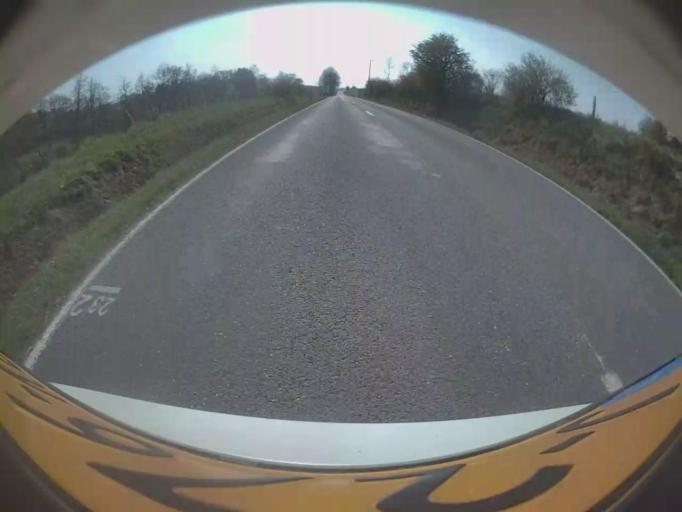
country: BE
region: Wallonia
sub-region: Province de Namur
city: Somme-Leuze
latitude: 50.3414
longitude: 5.3967
